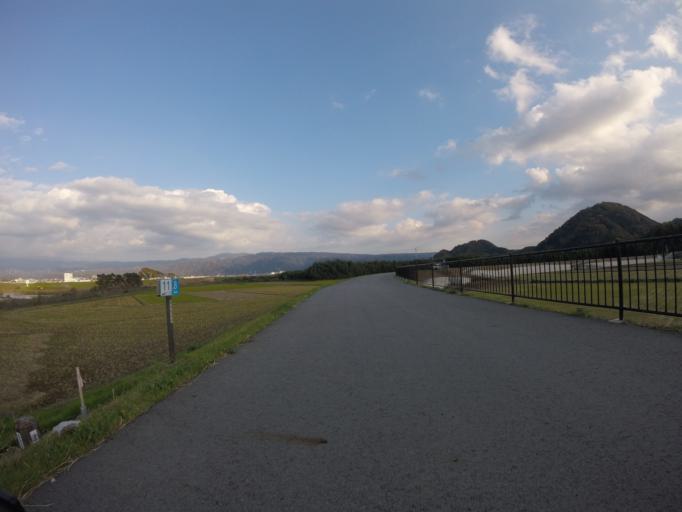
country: JP
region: Shizuoka
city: Mishima
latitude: 35.0740
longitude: 138.9205
